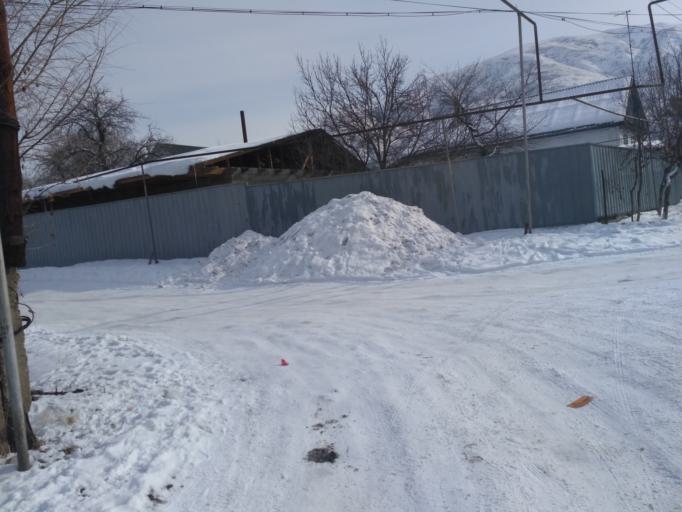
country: KZ
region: Almaty Oblysy
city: Burunday
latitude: 43.1588
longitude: 76.4040
